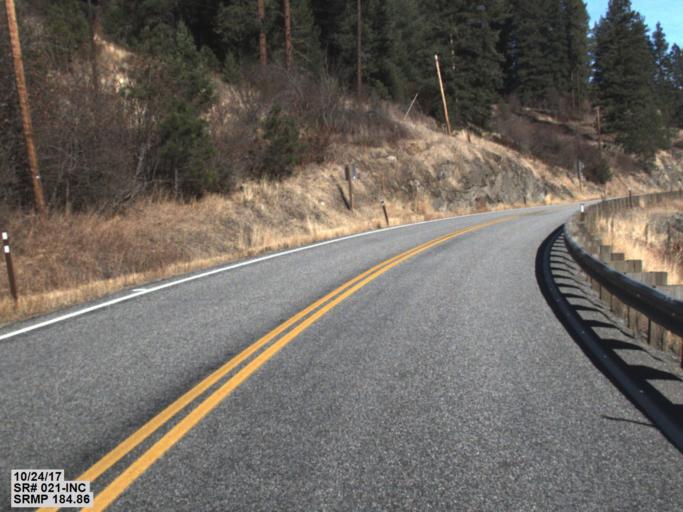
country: CA
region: British Columbia
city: Grand Forks
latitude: 48.9265
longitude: -118.5671
